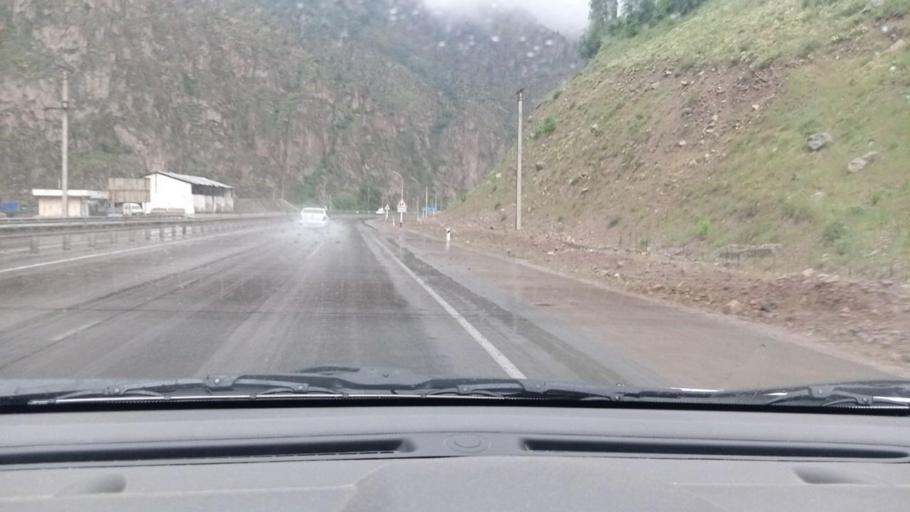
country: UZ
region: Toshkent
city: Angren
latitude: 41.1297
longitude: 70.3710
